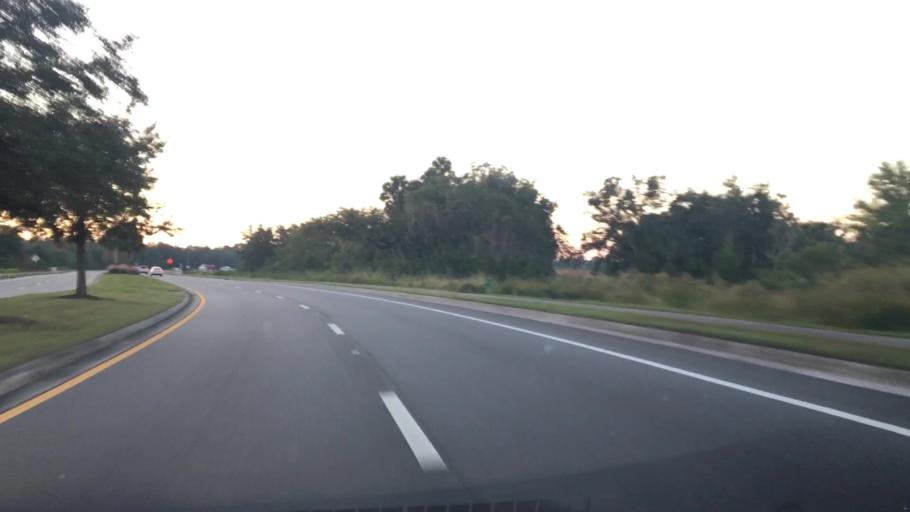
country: US
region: Florida
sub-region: Seminole County
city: Midway
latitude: 28.7843
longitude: -81.2125
